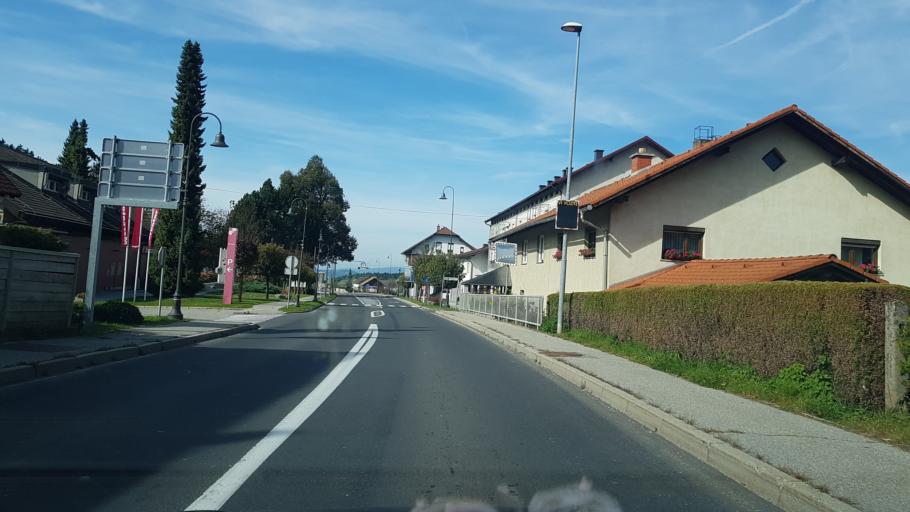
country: SI
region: Mislinja
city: Mislinja
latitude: 46.4421
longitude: 15.1951
